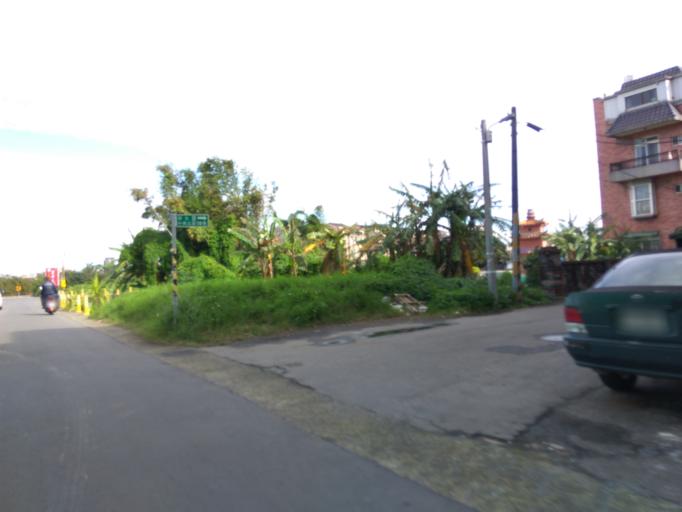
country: TW
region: Taiwan
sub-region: Hsinchu
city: Zhubei
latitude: 24.9758
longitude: 121.1034
